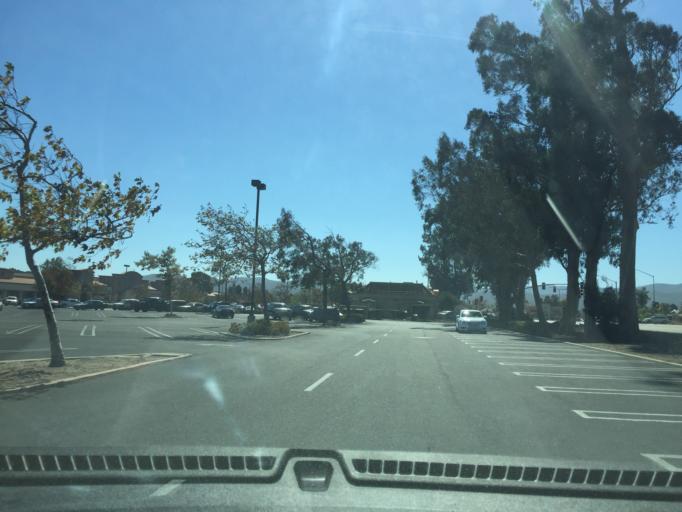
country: US
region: California
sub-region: Santa Barbara County
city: Lompoc
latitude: 34.6640
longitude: -120.4574
